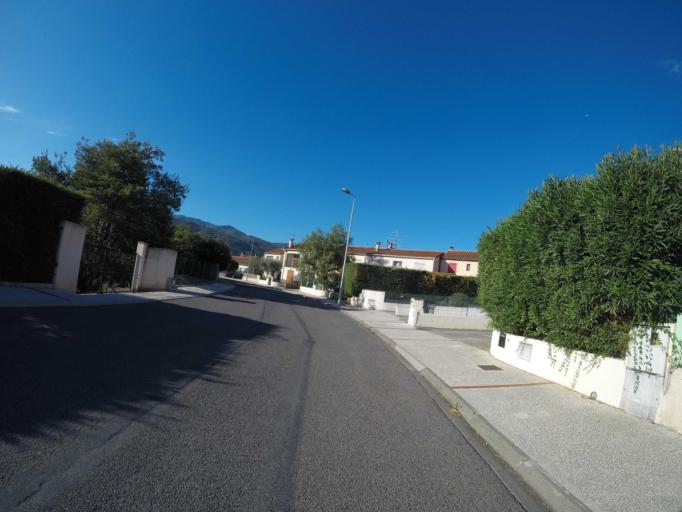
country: FR
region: Languedoc-Roussillon
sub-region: Departement des Pyrenees-Orientales
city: Ceret
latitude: 42.4997
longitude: 2.7471
